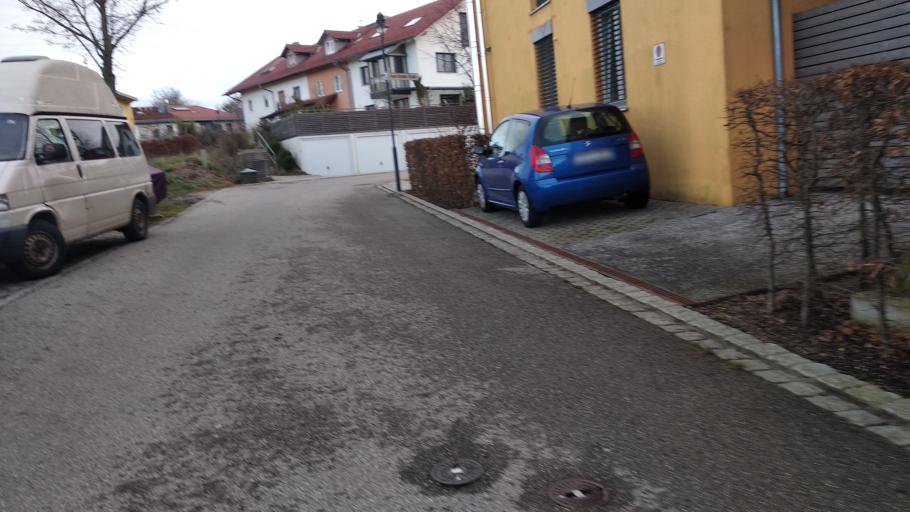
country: DE
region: Bavaria
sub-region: Upper Bavaria
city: Ebersberg
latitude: 48.0770
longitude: 11.9546
